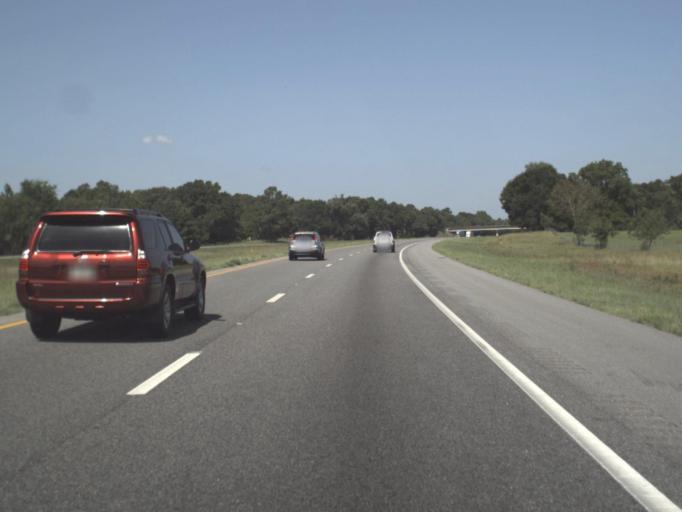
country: US
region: Florida
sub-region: Suwannee County
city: Live Oak
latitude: 30.3498
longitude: -83.0577
